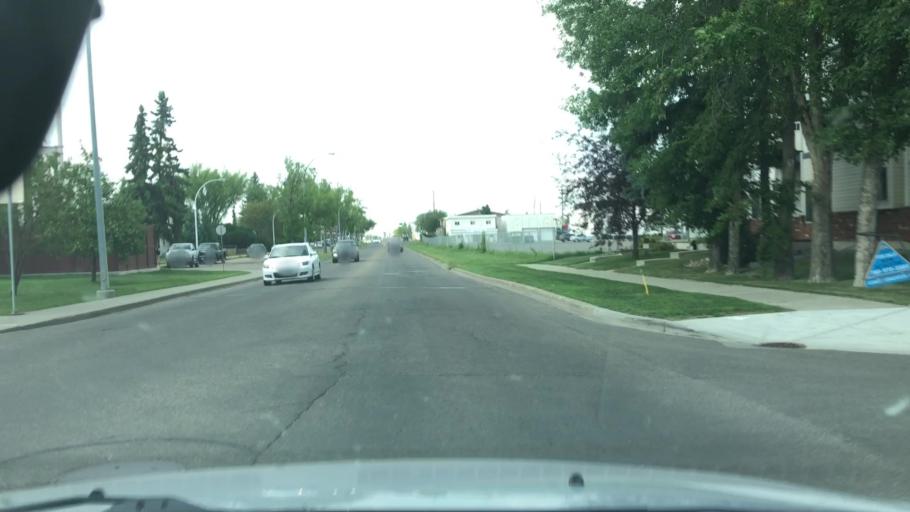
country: CA
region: Alberta
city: Edmonton
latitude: 53.5896
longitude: -113.5165
